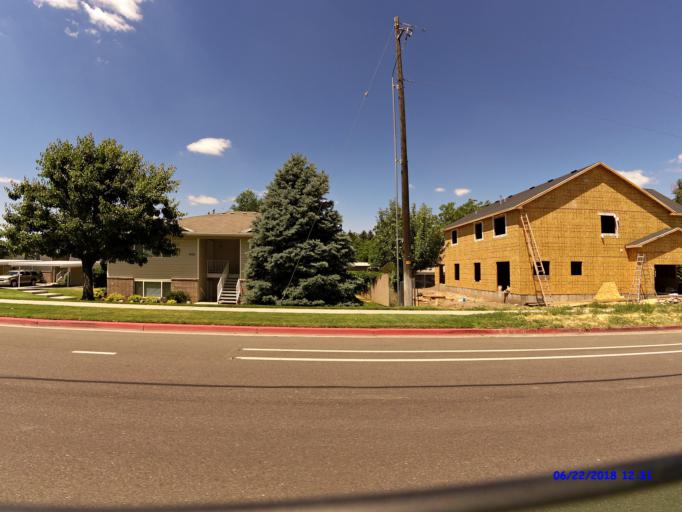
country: US
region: Utah
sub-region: Weber County
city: Ogden
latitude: 41.2409
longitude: -111.9528
